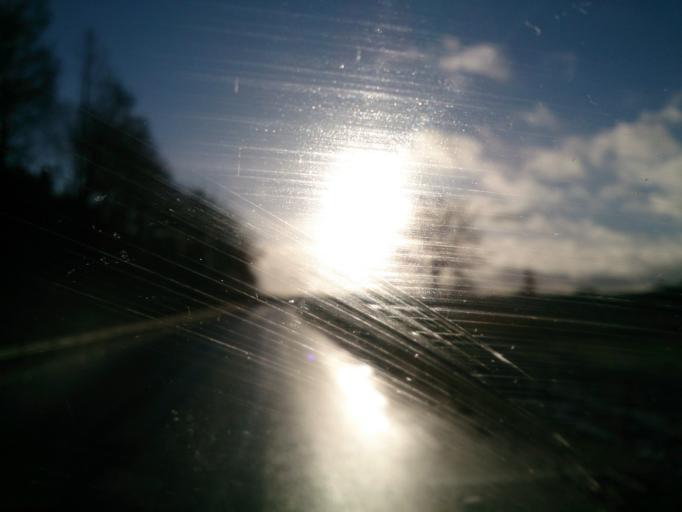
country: SE
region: OEstergoetland
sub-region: Atvidabergs Kommun
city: Atvidaberg
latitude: 58.2950
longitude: 15.8926
